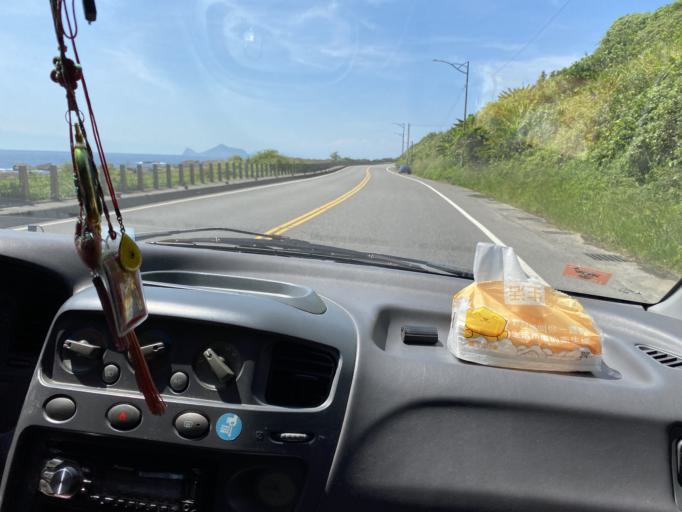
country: TW
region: Taiwan
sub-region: Keelung
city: Keelung
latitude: 24.9958
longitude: 121.9848
